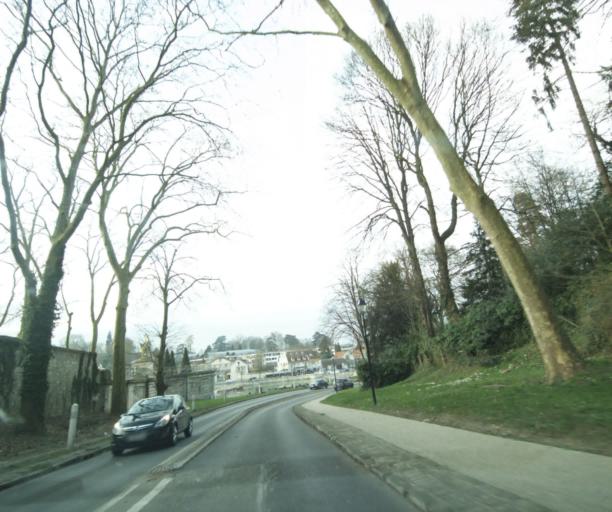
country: FR
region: Ile-de-France
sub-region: Departement des Yvelines
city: Louveciennes
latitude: 48.8658
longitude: 2.1022
